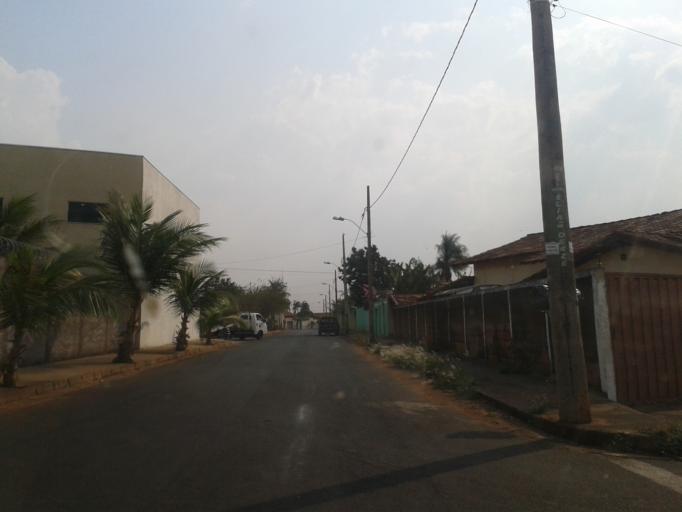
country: BR
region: Minas Gerais
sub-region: Ituiutaba
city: Ituiutaba
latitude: -18.9778
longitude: -49.4826
